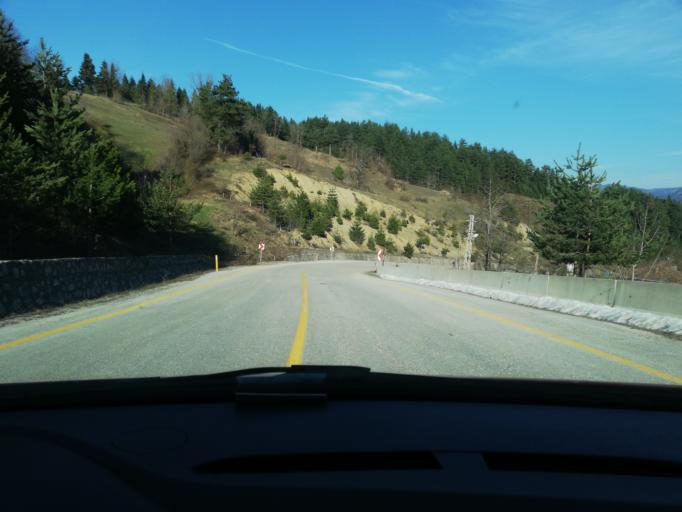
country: TR
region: Kastamonu
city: Senpazar
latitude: 41.7877
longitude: 33.1496
